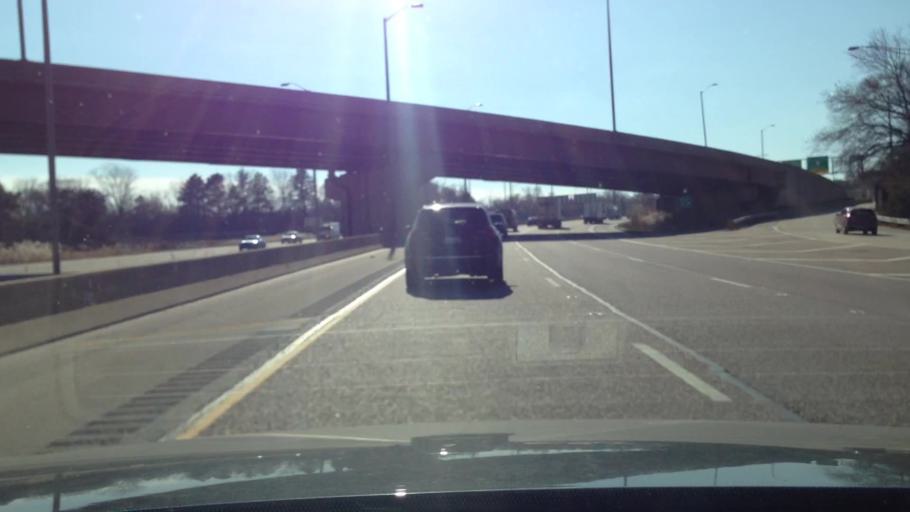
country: US
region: Illinois
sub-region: DuPage County
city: Itasca
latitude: 41.9588
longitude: -88.0268
